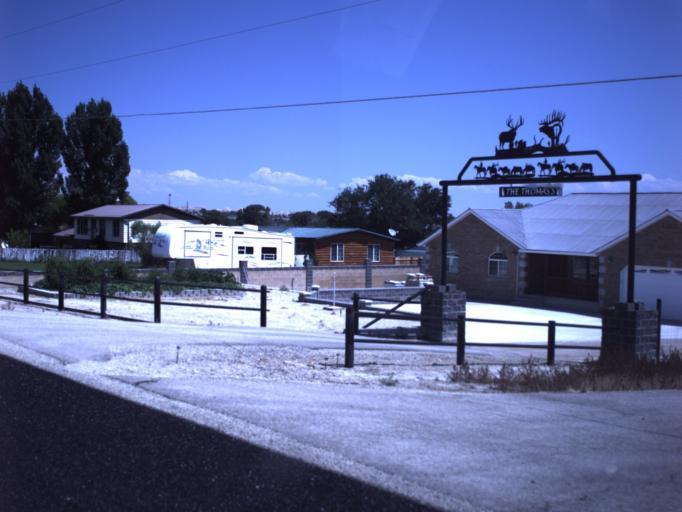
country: US
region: Utah
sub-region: Emery County
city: Ferron
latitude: 39.0689
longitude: -111.1315
